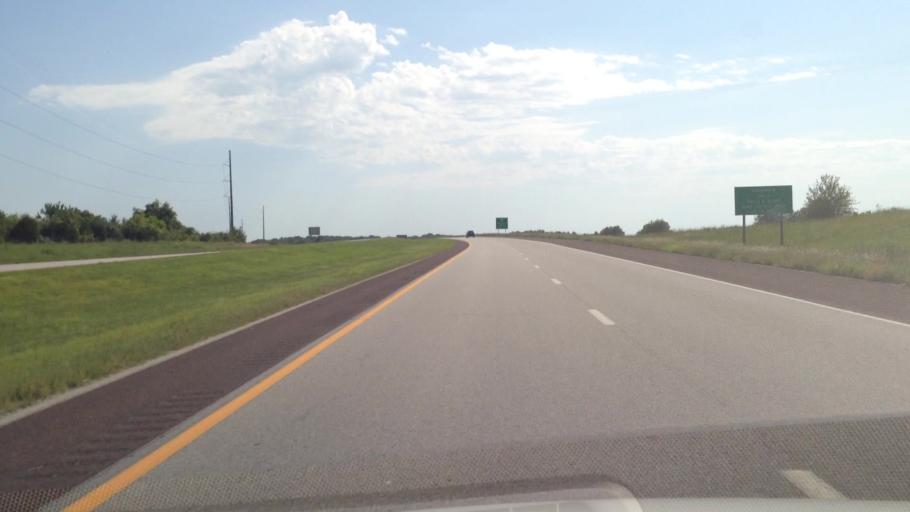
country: US
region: Kansas
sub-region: Miami County
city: Louisburg
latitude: 38.6400
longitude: -94.6925
